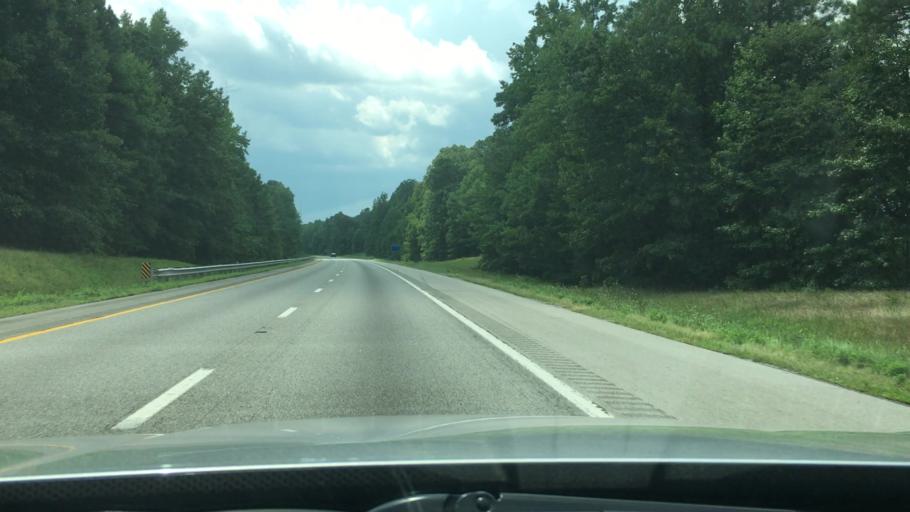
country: US
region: Virginia
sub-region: City of Emporia
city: Emporia
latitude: 36.7571
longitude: -77.5046
